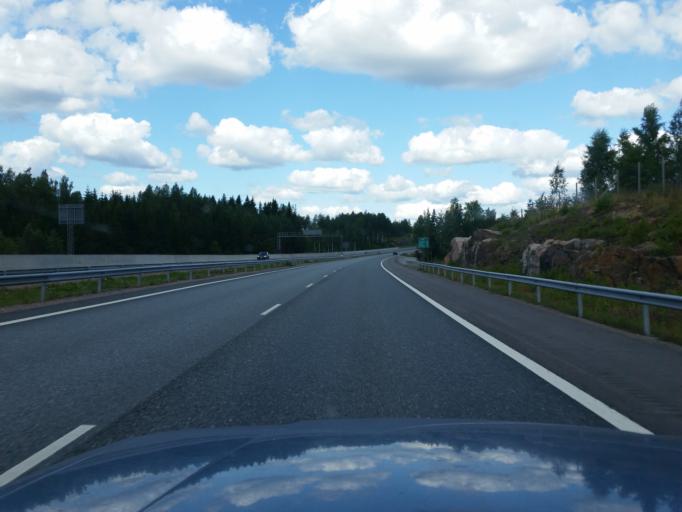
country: FI
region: Uusimaa
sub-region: Helsinki
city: Sammatti
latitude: 60.3501
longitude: 23.8979
